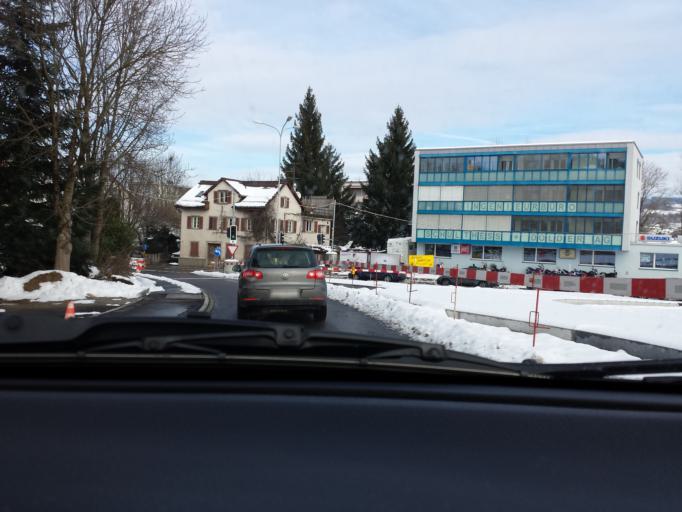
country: CH
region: Zurich
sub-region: Bezirk Hinwil
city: Wetzikon / Unter-Wetzikon
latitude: 47.3155
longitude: 8.7958
